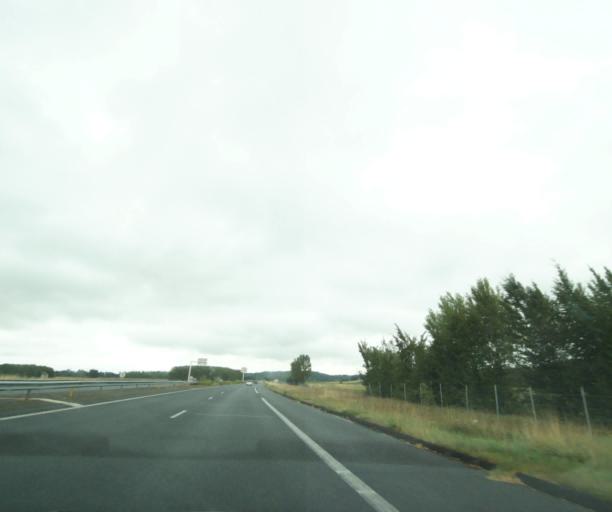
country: FR
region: Midi-Pyrenees
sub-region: Departement du Tarn
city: Lagrave
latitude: 43.8884
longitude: 1.9751
